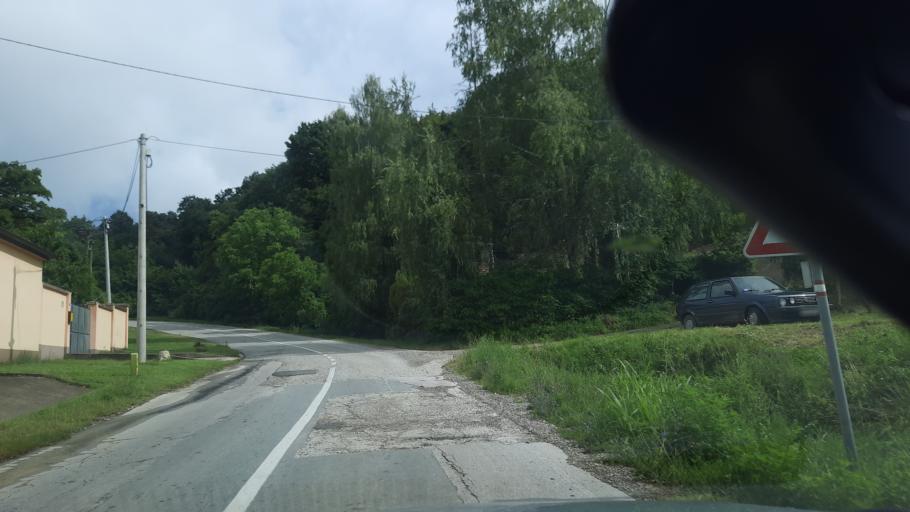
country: RS
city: Glozan
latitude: 45.1375
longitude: 19.5807
